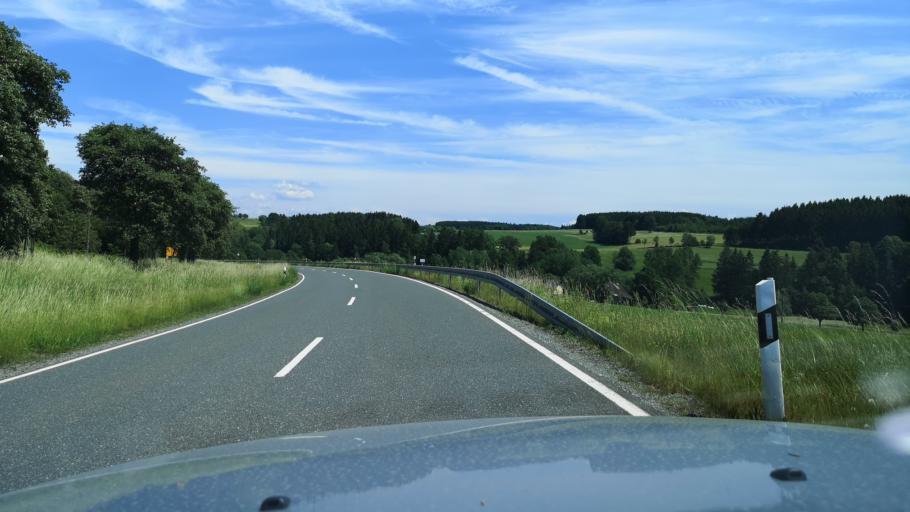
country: DE
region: Bavaria
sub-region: Upper Franconia
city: Teuschnitz
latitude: 50.3885
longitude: 11.3756
